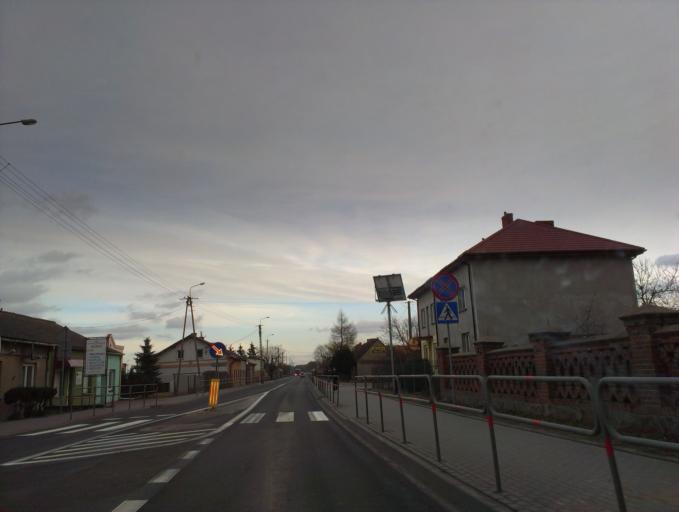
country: PL
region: Masovian Voivodeship
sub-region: Powiat sierpecki
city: Szczutowo
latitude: 52.9015
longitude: 19.5271
